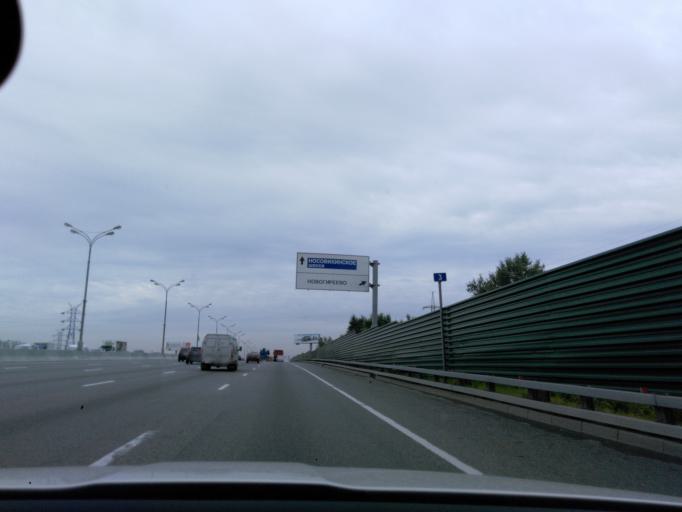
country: RU
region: Moscow
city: Ivanovskoye
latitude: 55.7520
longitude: 37.8419
